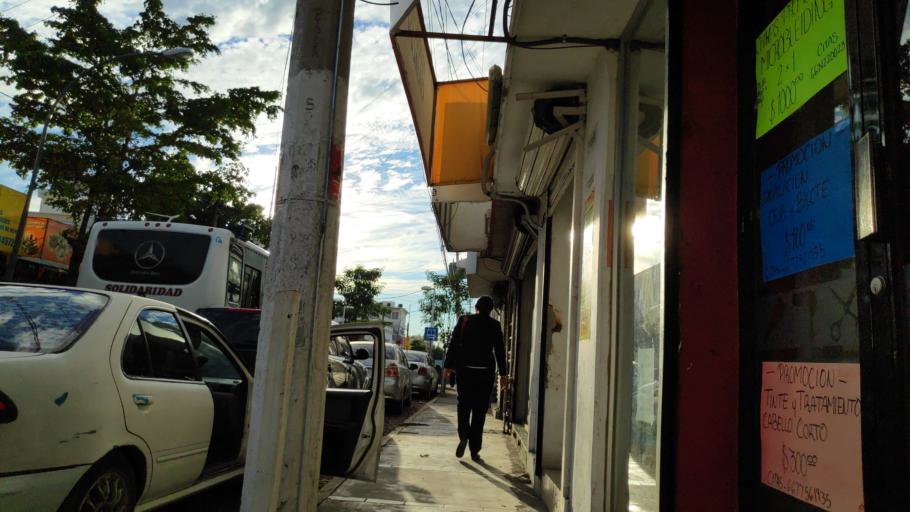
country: MX
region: Sinaloa
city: Culiacan
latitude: 24.8104
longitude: -107.3981
